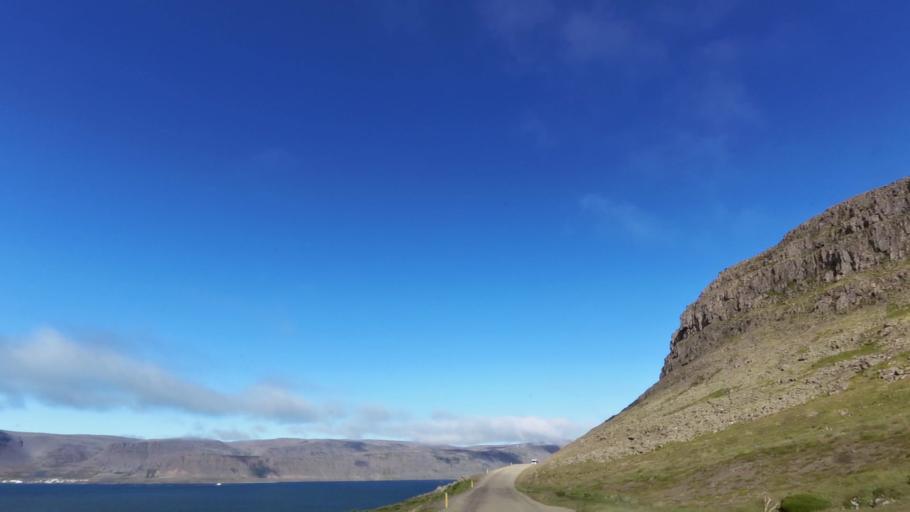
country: IS
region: West
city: Olafsvik
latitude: 65.5613
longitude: -24.0306
